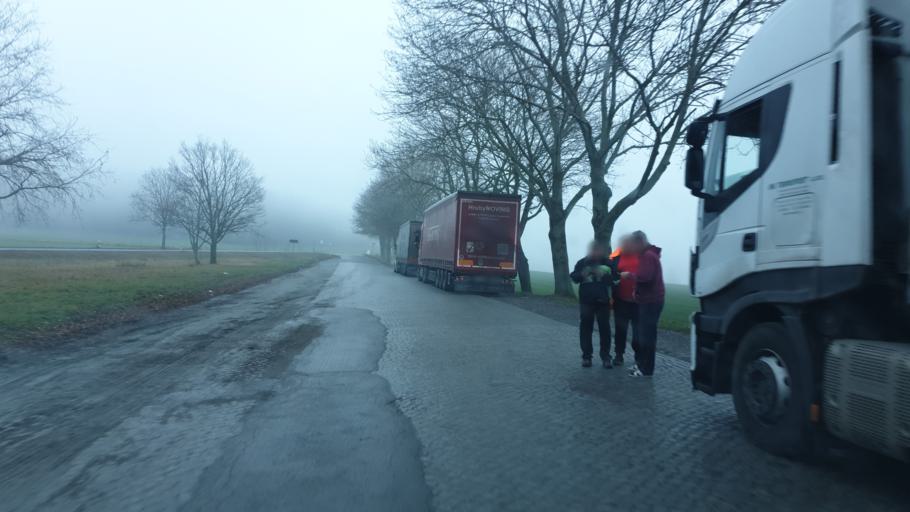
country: DE
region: Saxony
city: Grossolbersdorf
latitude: 50.6997
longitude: 13.1097
